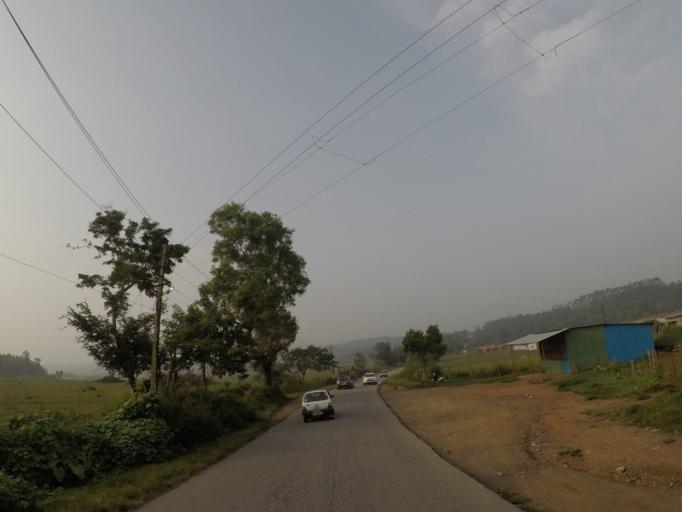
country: IN
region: Karnataka
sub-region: Chikmagalur
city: Mudigere
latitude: 13.2522
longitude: 75.6619
